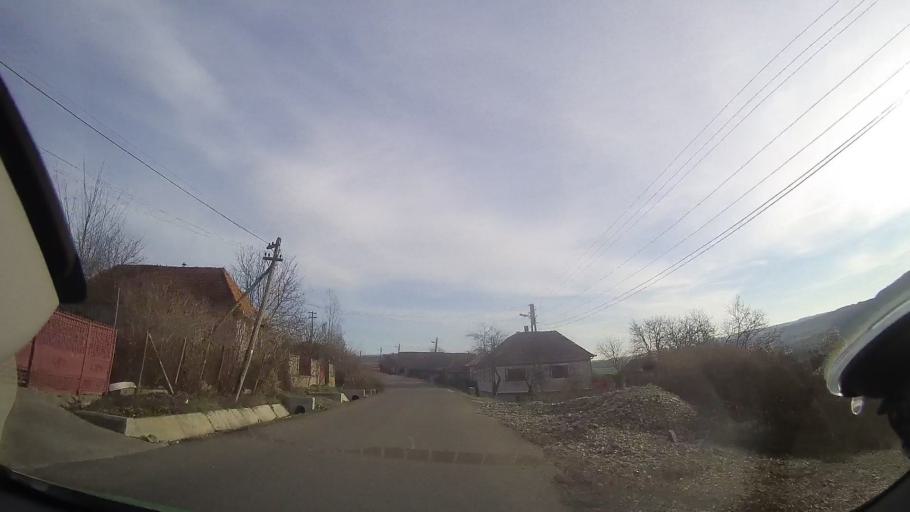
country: RO
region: Bihor
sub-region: Comuna Sarbi
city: Burzuc
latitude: 47.1726
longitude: 22.1546
